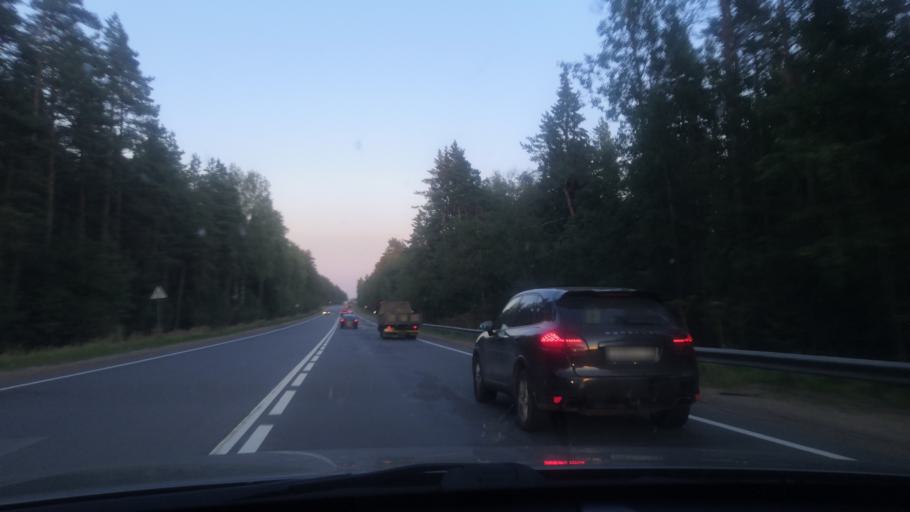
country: RU
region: St.-Petersburg
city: Solnechnoye
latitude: 60.2030
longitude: 29.9597
